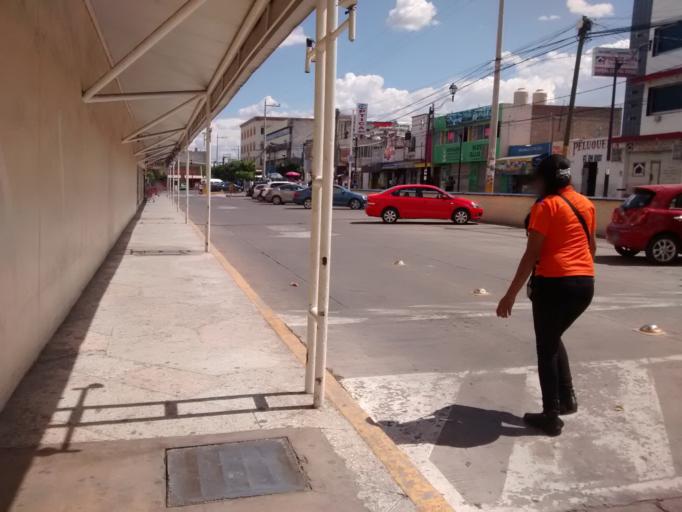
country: MX
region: Puebla
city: Tehuacan
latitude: 18.4641
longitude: -97.3868
